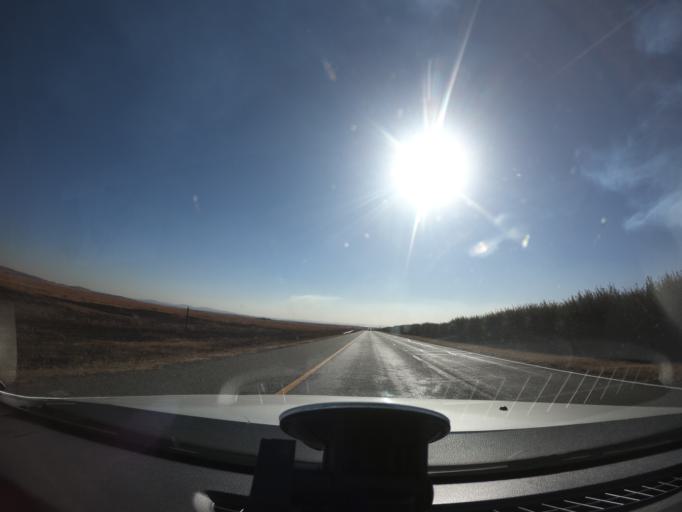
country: ZA
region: Gauteng
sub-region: Sedibeng District Municipality
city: Heidelberg
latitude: -26.4345
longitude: 28.2988
